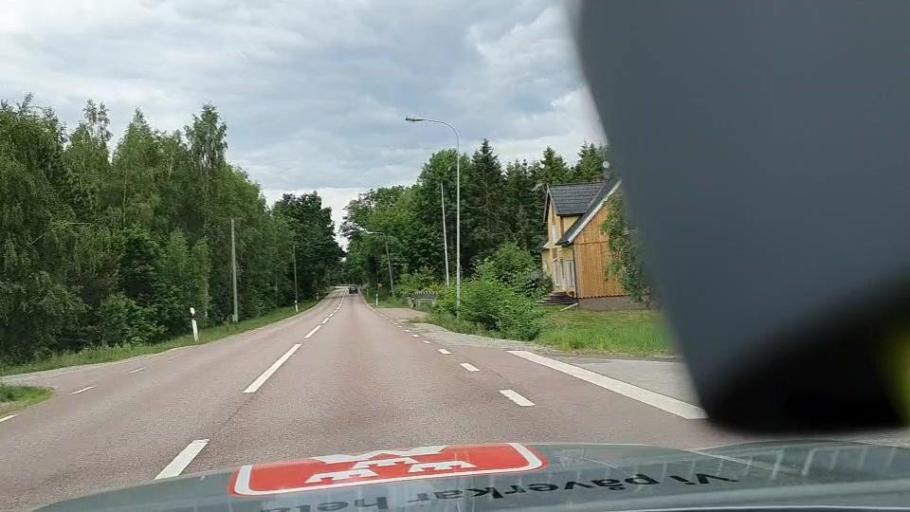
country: SE
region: Kalmar
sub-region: Emmaboda Kommun
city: Emmaboda
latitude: 56.4604
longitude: 15.5899
